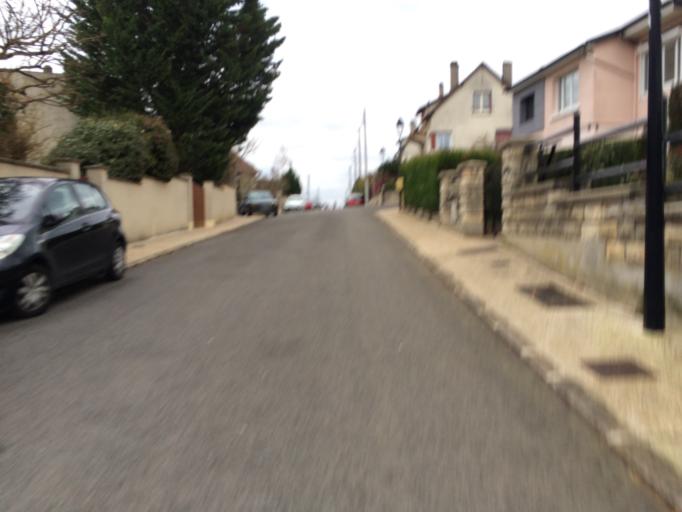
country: FR
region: Ile-de-France
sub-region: Departement de l'Essonne
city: Vauhallan
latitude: 48.7323
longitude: 2.2128
